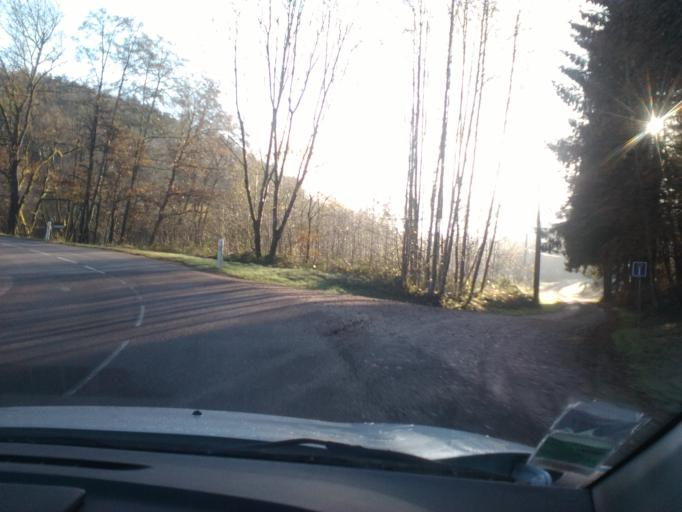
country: FR
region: Lorraine
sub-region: Departement des Vosges
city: Uzemain
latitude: 48.0694
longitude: 6.3133
